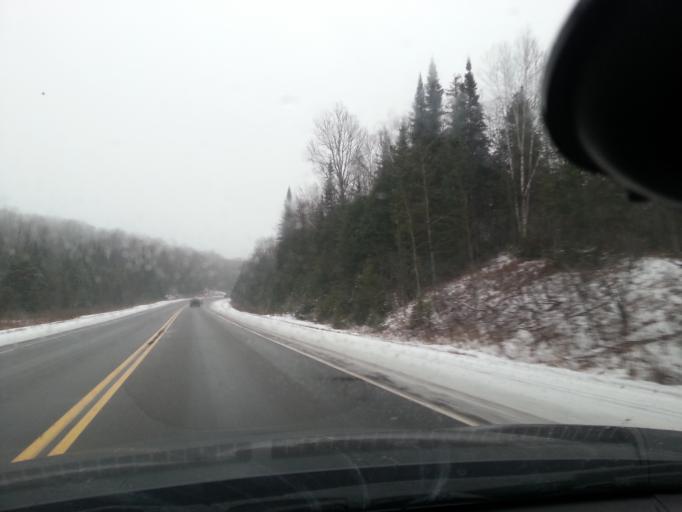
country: CA
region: Ontario
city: Perth
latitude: 44.7628
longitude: -76.7657
